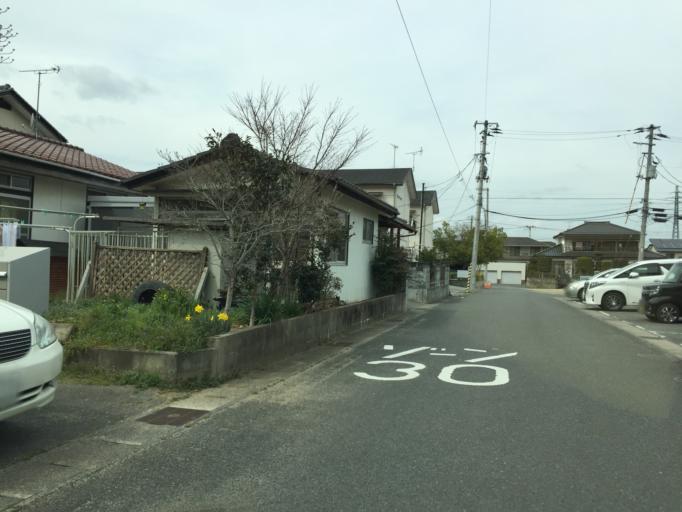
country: JP
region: Fukushima
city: Iwaki
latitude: 37.0440
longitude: 140.9064
